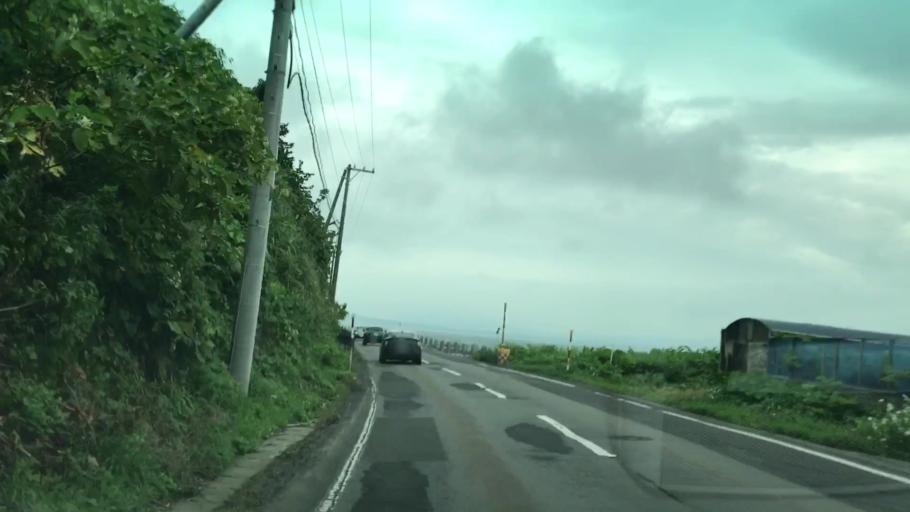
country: JP
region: Hokkaido
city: Iwanai
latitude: 42.8126
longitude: 140.3040
